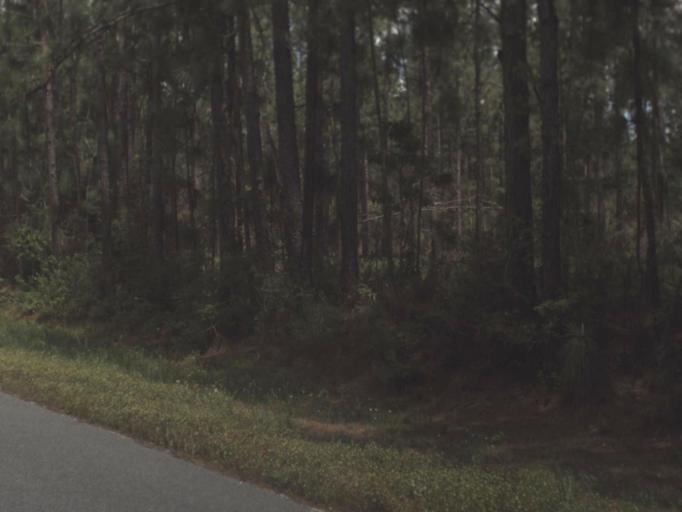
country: US
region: Florida
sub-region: Escambia County
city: Molino
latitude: 30.8240
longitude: -87.4356
